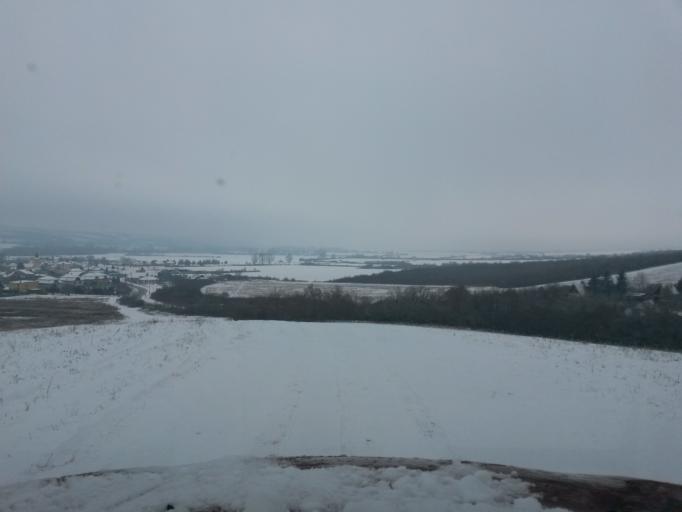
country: SK
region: Kosicky
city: Kosice
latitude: 48.7130
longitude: 21.3232
